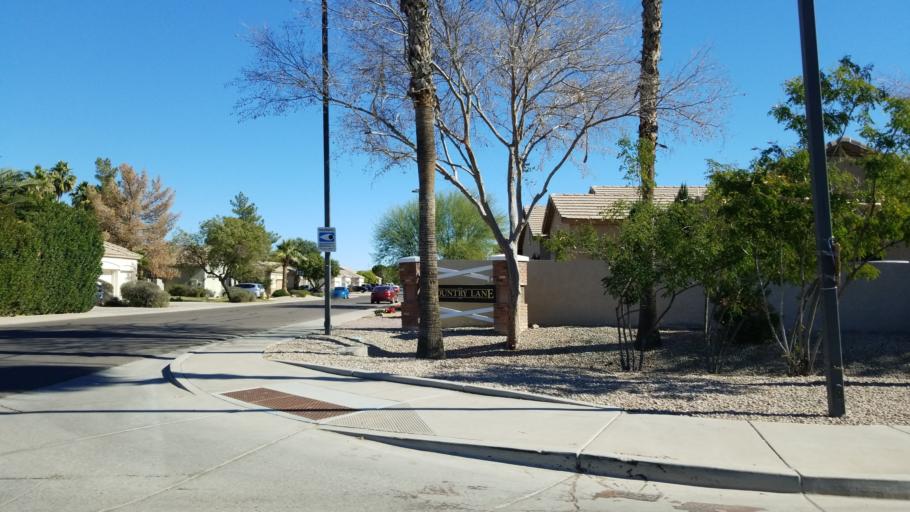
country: US
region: Arizona
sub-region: Maricopa County
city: Gilbert
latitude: 33.3415
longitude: -111.7897
